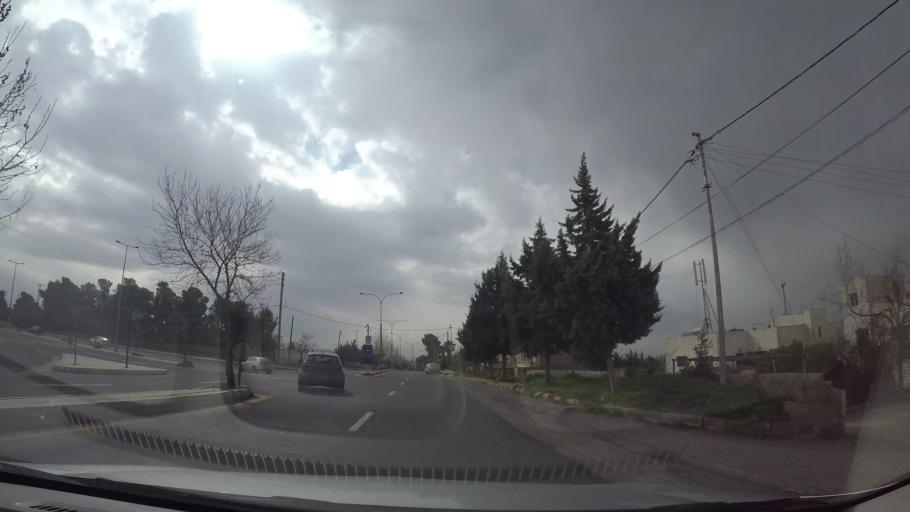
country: JO
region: Amman
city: Wadi as Sir
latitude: 31.9803
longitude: 35.8221
